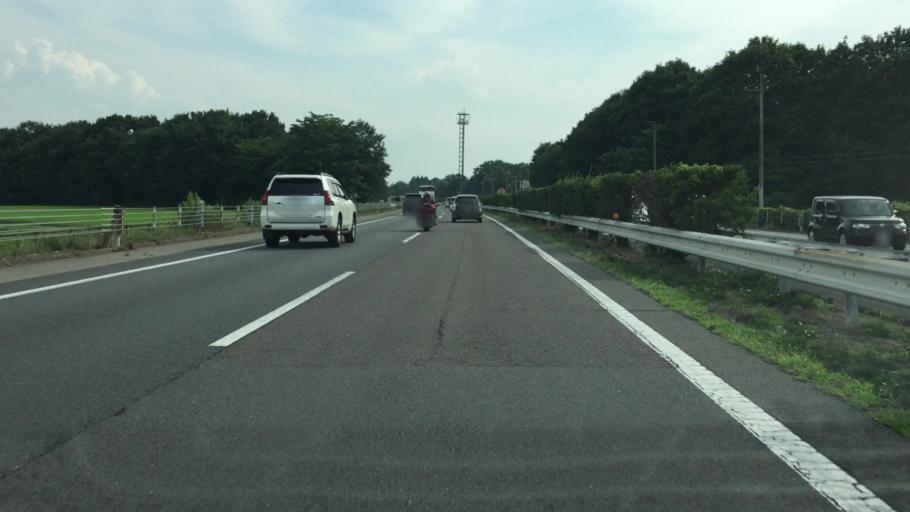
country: JP
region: Tochigi
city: Yaita
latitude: 36.9064
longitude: 139.9318
